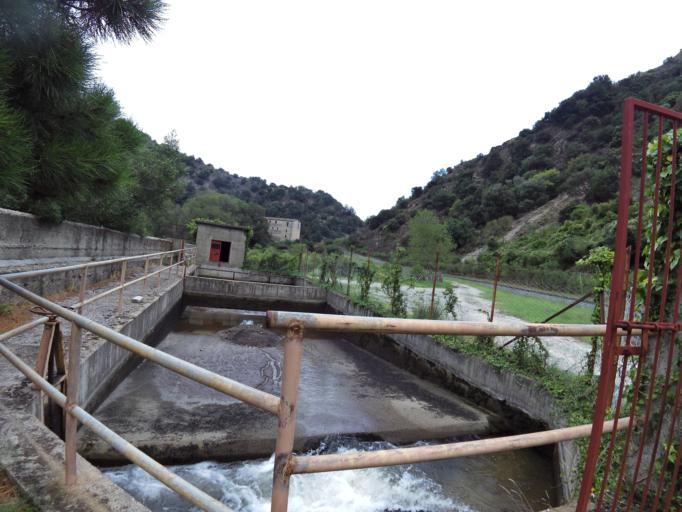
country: IT
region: Calabria
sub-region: Provincia di Reggio Calabria
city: Caulonia
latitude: 38.4253
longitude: 16.3758
